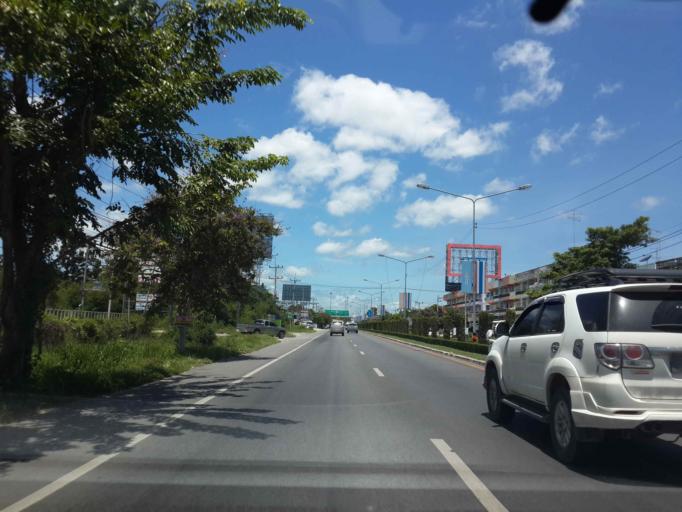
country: TH
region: Phetchaburi
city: Cha-am
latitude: 12.8055
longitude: 99.9505
